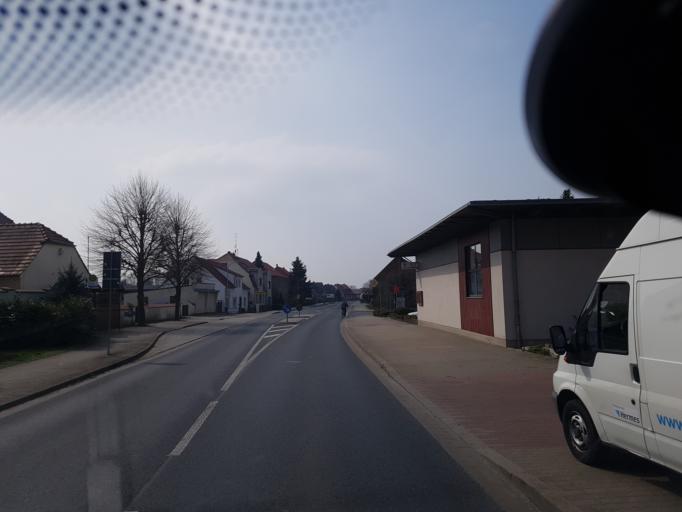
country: DE
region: Brandenburg
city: Schlieben
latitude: 51.7222
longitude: 13.3834
